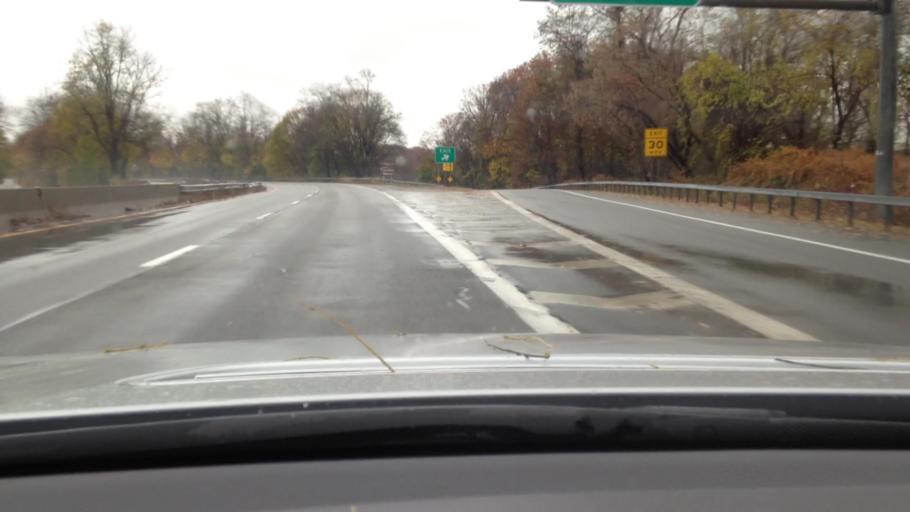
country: US
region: New York
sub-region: Westchester County
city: Buchanan
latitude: 41.2725
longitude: -73.9335
